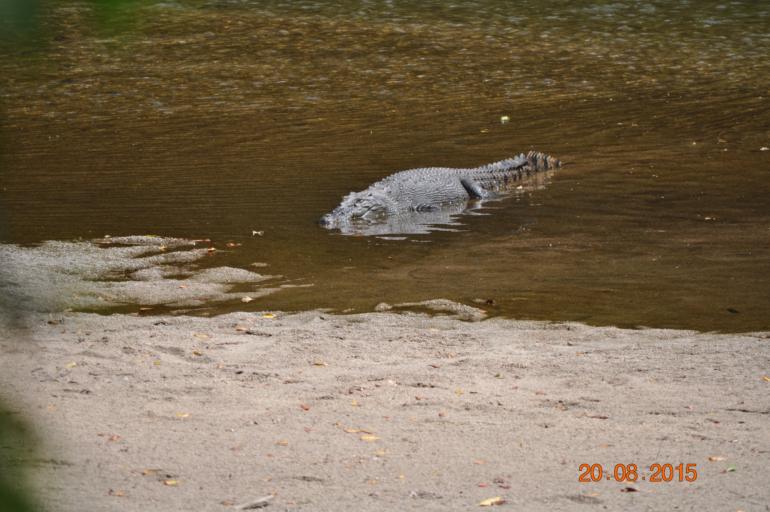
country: AU
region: Queensland
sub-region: Cairns
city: Woree
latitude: -17.1366
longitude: 145.8745
